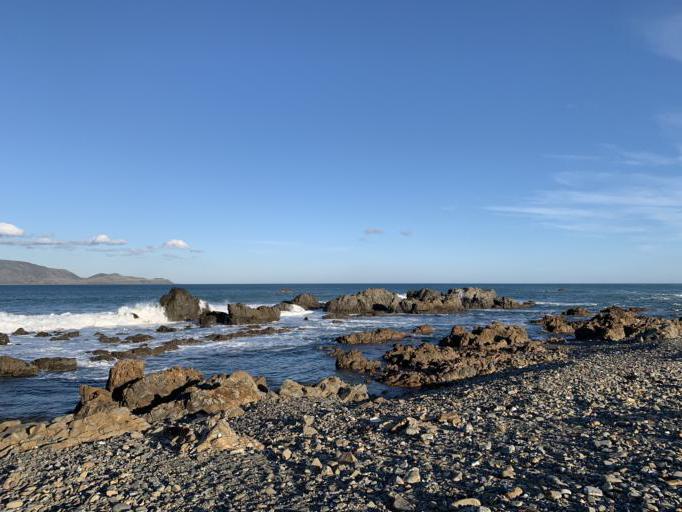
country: NZ
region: Wellington
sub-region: Wellington City
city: Wellington
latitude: -41.3443
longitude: 174.8211
